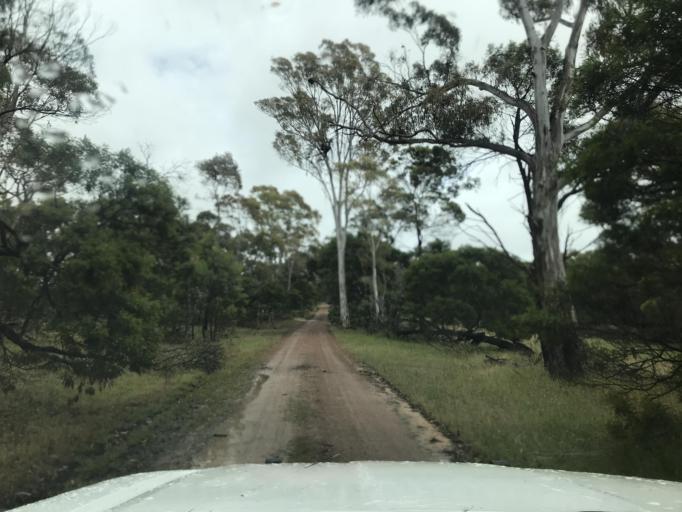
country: AU
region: South Australia
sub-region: Wattle Range
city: Penola
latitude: -37.2645
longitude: 141.3121
